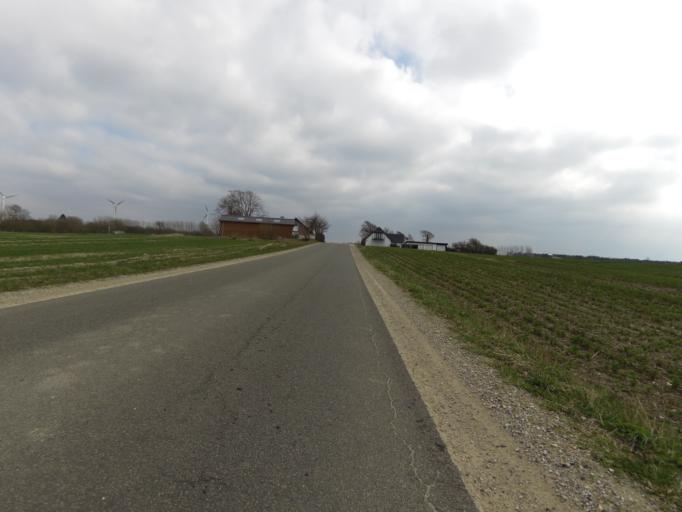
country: DK
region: Central Jutland
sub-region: Holstebro Kommune
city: Holstebro
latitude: 56.4315
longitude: 8.6825
